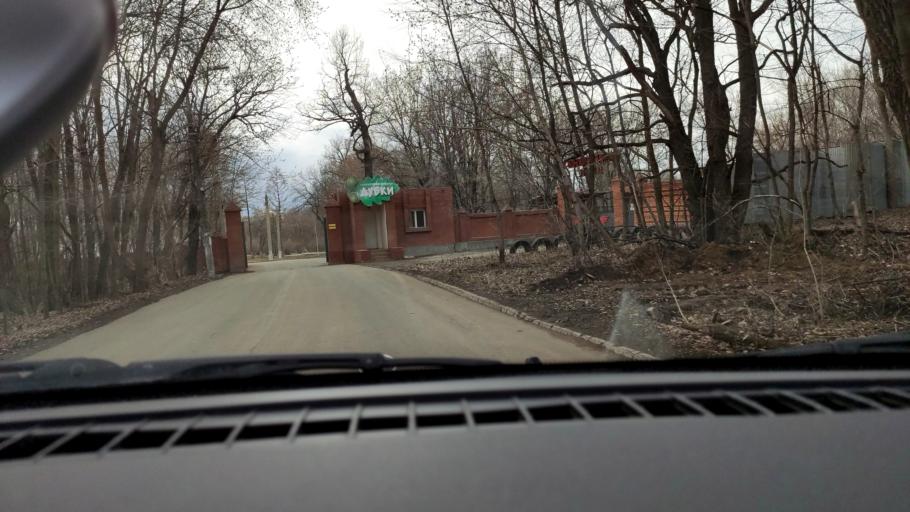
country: RU
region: Samara
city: Samara
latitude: 53.2749
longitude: 50.2222
